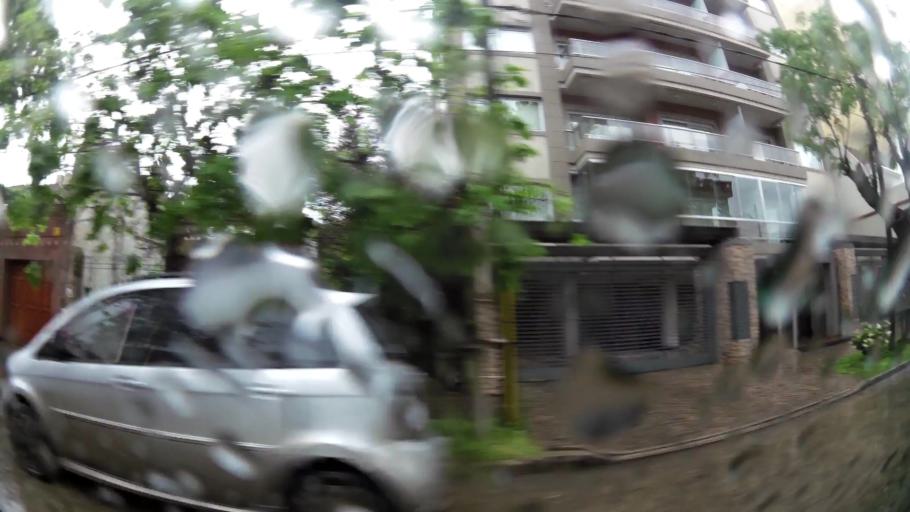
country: AR
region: Buenos Aires
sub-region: Partido de Lanus
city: Lanus
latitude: -34.7159
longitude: -58.3957
